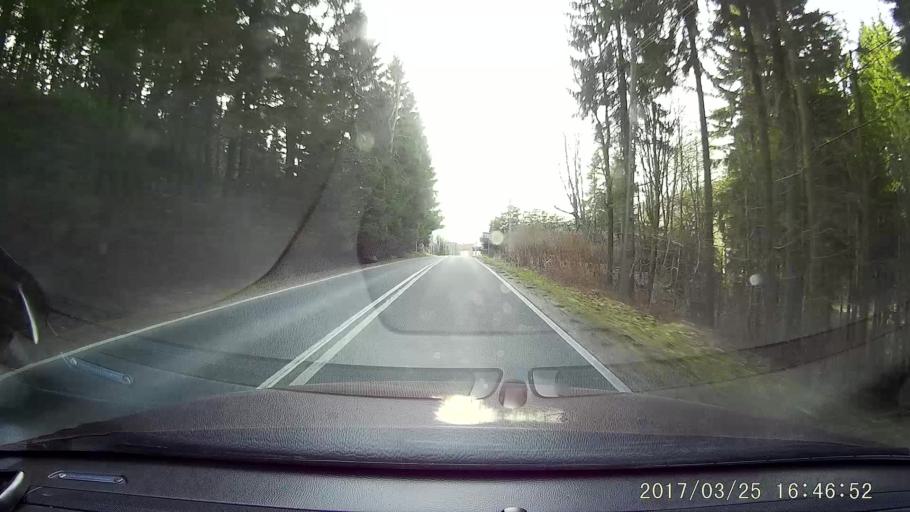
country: PL
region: Lower Silesian Voivodeship
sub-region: Powiat lubanski
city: Swieradow-Zdroj
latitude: 50.8913
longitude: 15.3751
